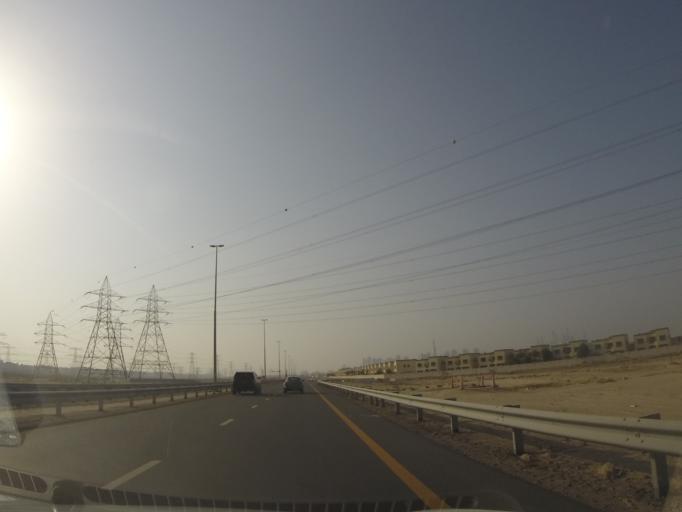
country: AE
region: Dubai
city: Dubai
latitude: 25.0372
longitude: 55.1608
